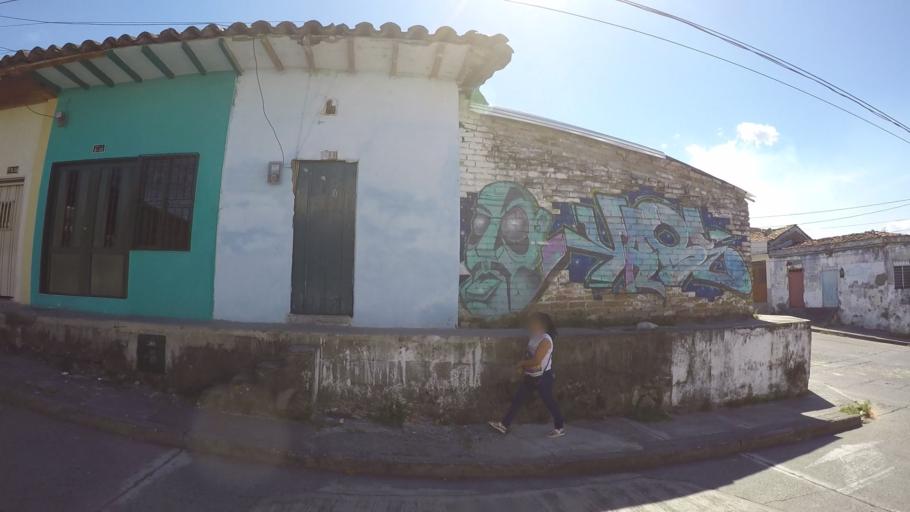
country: CO
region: Valle del Cauca
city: Cartago
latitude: 4.7524
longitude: -75.9037
